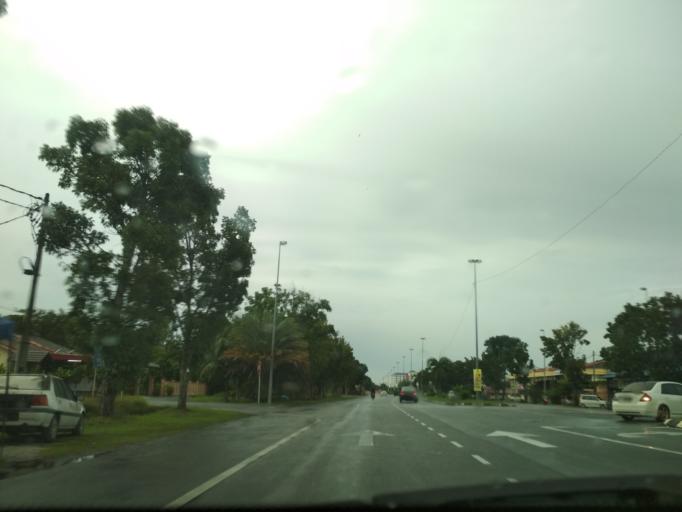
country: MY
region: Perlis
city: Kangar
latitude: 6.4220
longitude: 100.1840
